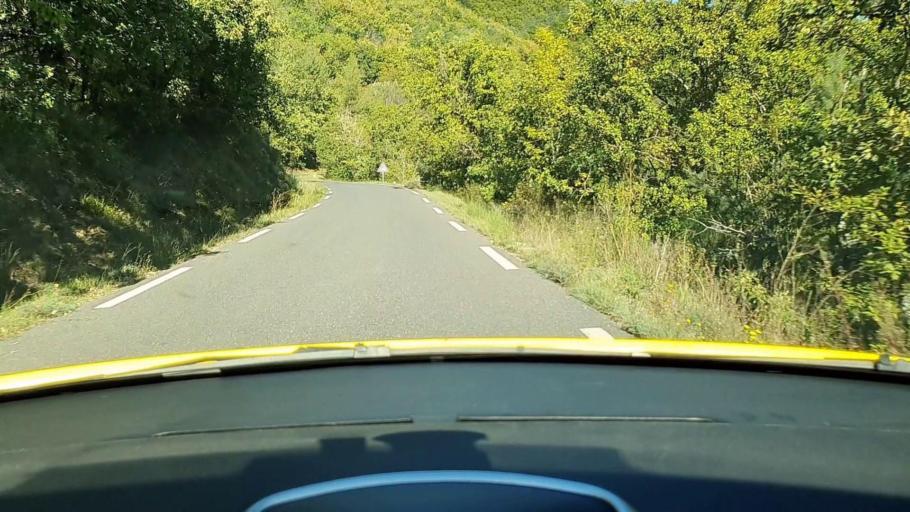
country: FR
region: Languedoc-Roussillon
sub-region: Departement du Gard
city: Le Vigan
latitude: 43.9705
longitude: 3.4510
